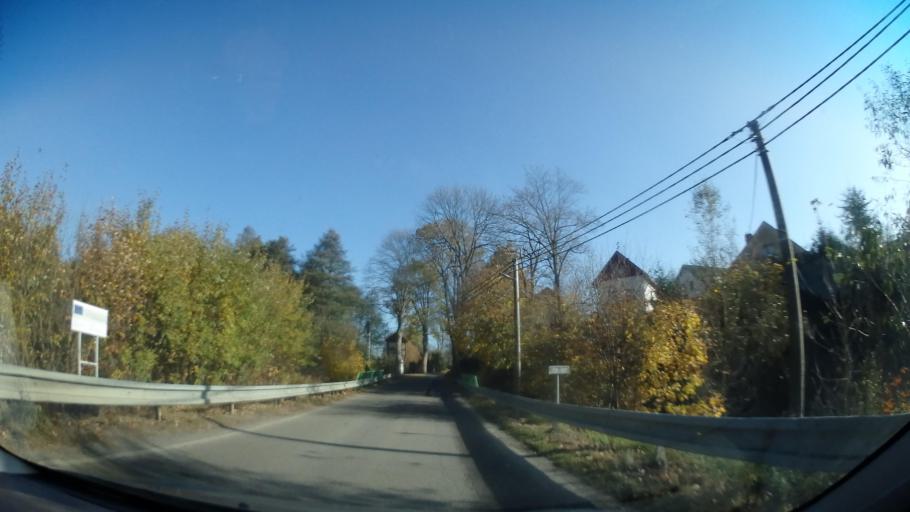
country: CZ
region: Vysocina
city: Zd'ar nad Sazavou Druhy
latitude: 49.6085
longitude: 15.9162
